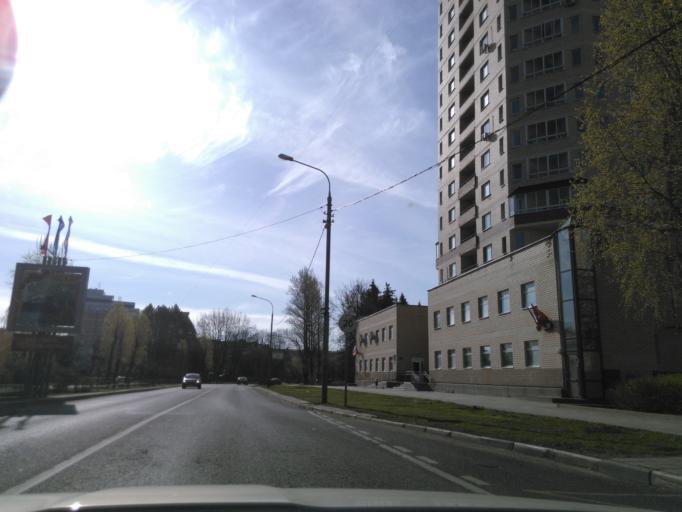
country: RU
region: Moskovskaya
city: Rzhavki
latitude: 55.9996
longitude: 37.2191
